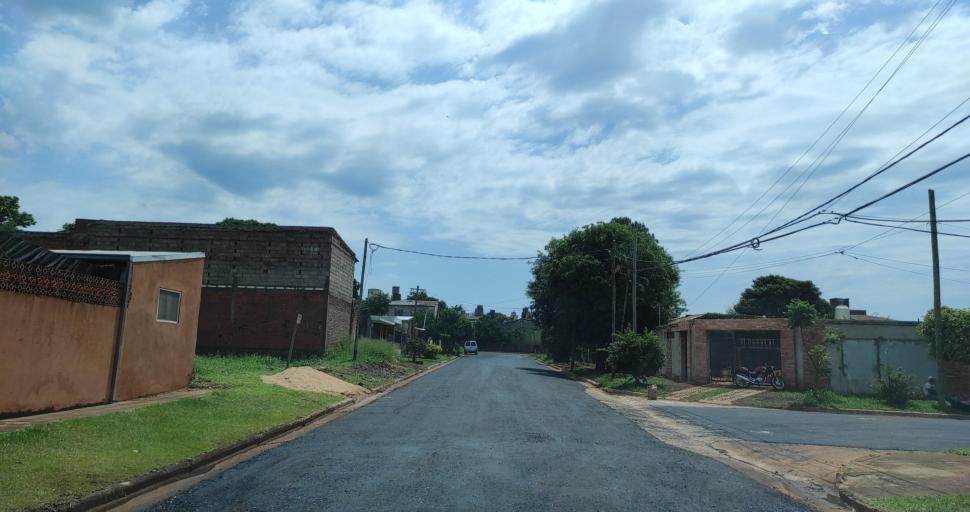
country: AR
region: Misiones
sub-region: Departamento de Capital
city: Posadas
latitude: -27.3686
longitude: -55.9421
